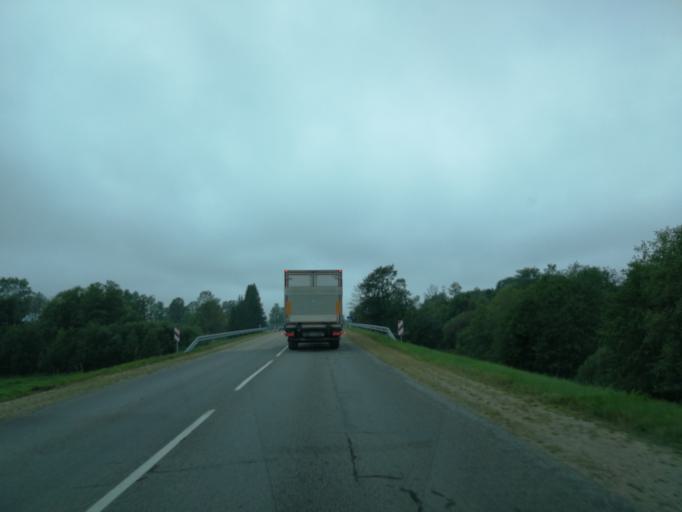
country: LV
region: Livani
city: Livani
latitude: 56.3414
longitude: 26.3486
